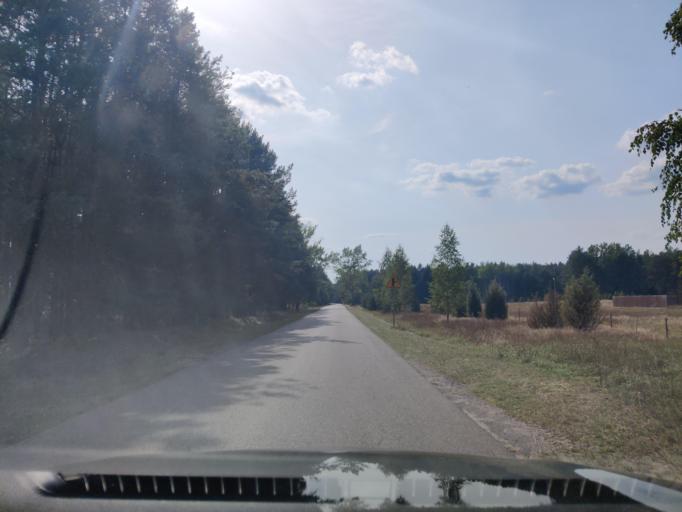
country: PL
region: Masovian Voivodeship
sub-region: Powiat wyszkowski
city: Dlugosiodlo
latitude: 52.7767
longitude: 21.4895
